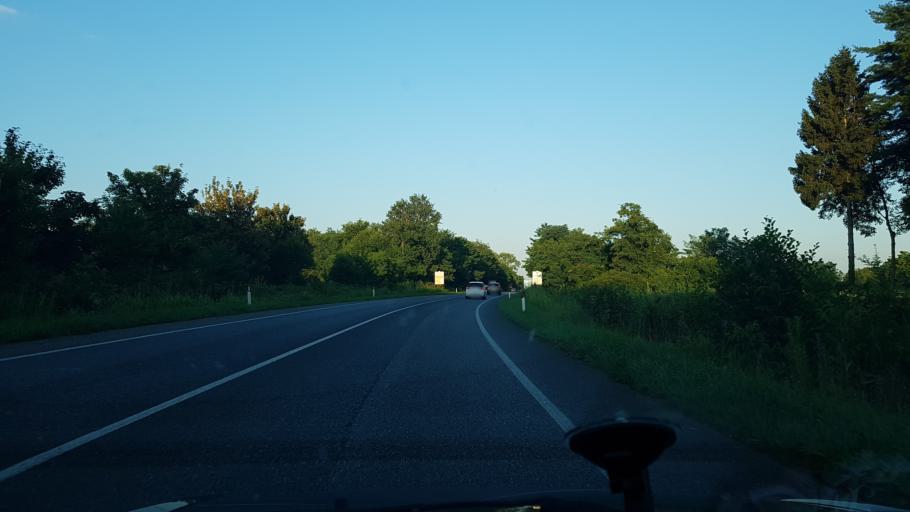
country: IT
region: Friuli Venezia Giulia
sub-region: Provincia di Udine
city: Passons
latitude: 46.0860
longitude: 13.1705
